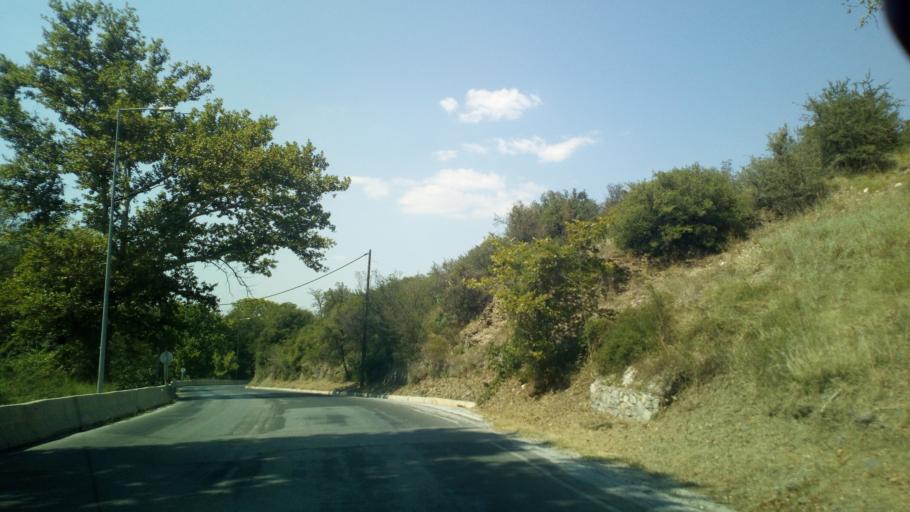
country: GR
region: Central Macedonia
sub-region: Nomos Thessalonikis
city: Asvestochori
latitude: 40.6361
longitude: 23.0366
